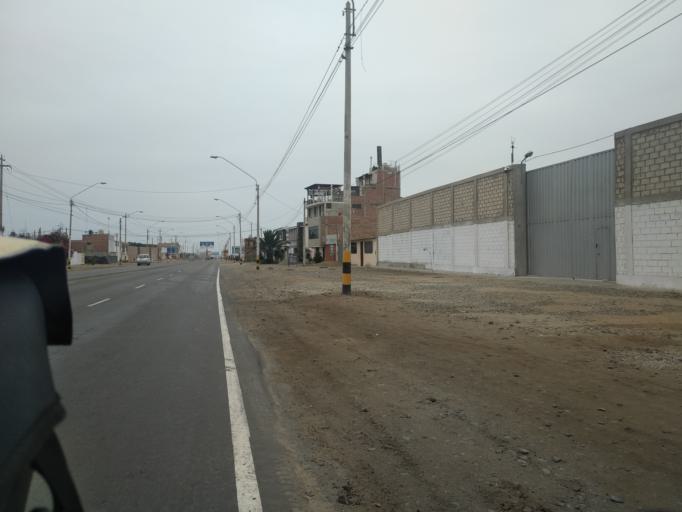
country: PE
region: La Libertad
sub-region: Provincia de Trujillo
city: Huanchaco
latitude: -8.0891
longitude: -79.1028
